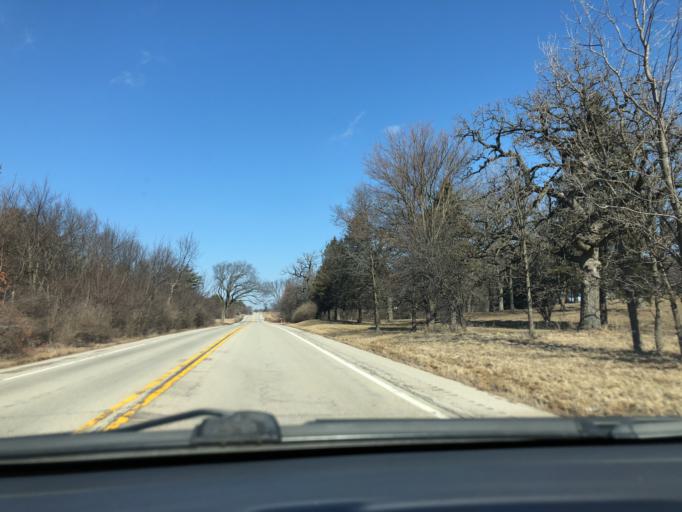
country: US
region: Illinois
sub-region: Kane County
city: Hampshire
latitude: 42.1041
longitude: -88.4815
